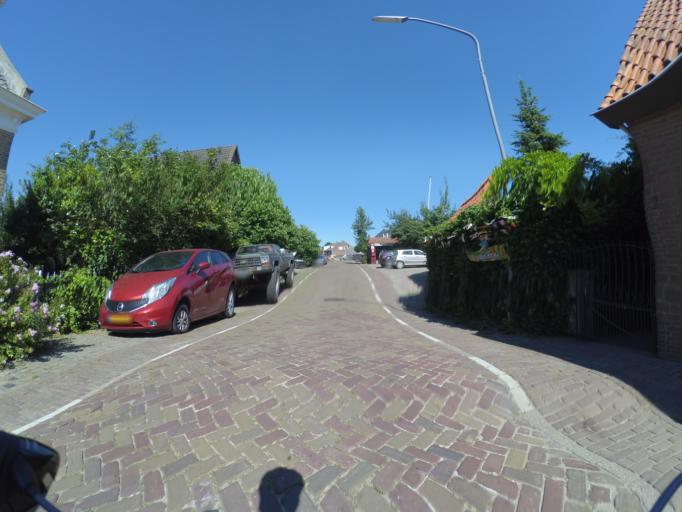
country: NL
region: North Brabant
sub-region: Gemeente Made en Drimmelen
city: Made
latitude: 51.7091
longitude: 4.7078
